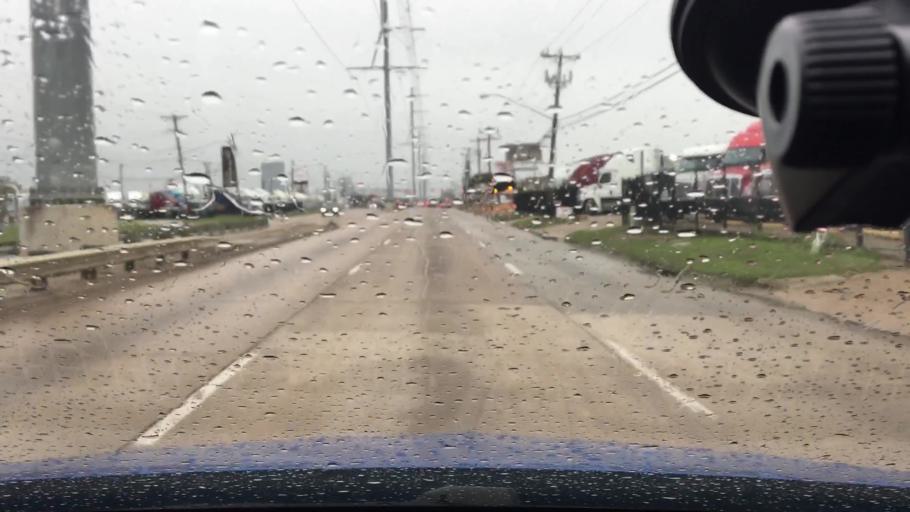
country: US
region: Texas
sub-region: Dallas County
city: Irving
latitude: 32.8080
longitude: -96.8767
